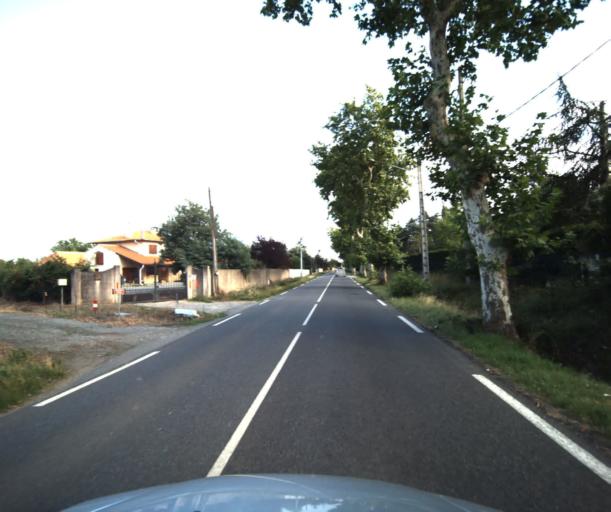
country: FR
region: Midi-Pyrenees
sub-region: Departement de la Haute-Garonne
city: Muret
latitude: 43.4466
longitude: 1.3376
